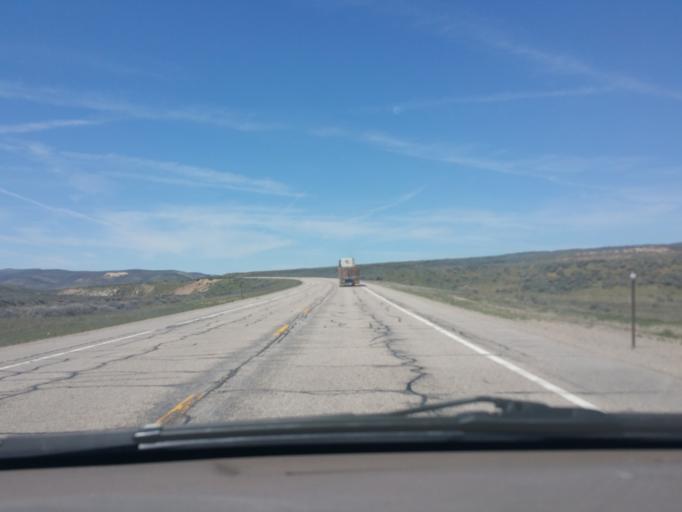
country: US
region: Wyoming
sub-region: Lincoln County
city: Kemmerer
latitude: 41.8156
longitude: -110.6600
